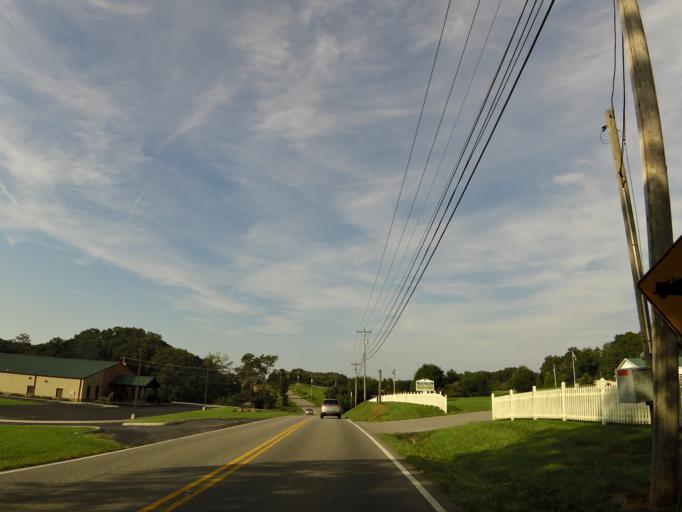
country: US
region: Tennessee
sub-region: Blount County
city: Wildwood
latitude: 35.8353
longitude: -83.7935
